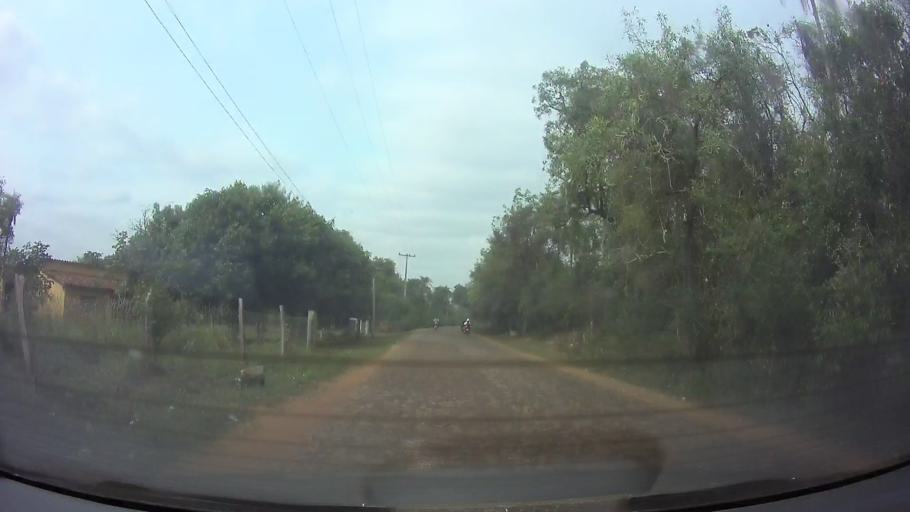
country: PY
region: Cordillera
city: Arroyos y Esteros
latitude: -25.0281
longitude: -57.1098
